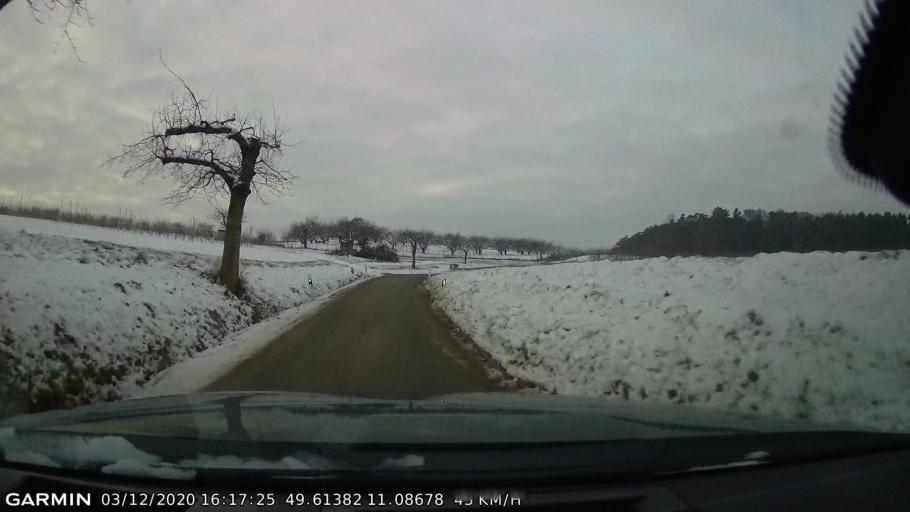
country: DE
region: Bavaria
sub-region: Regierungsbezirk Mittelfranken
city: Uttenreuth
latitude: 49.6138
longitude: 11.0868
